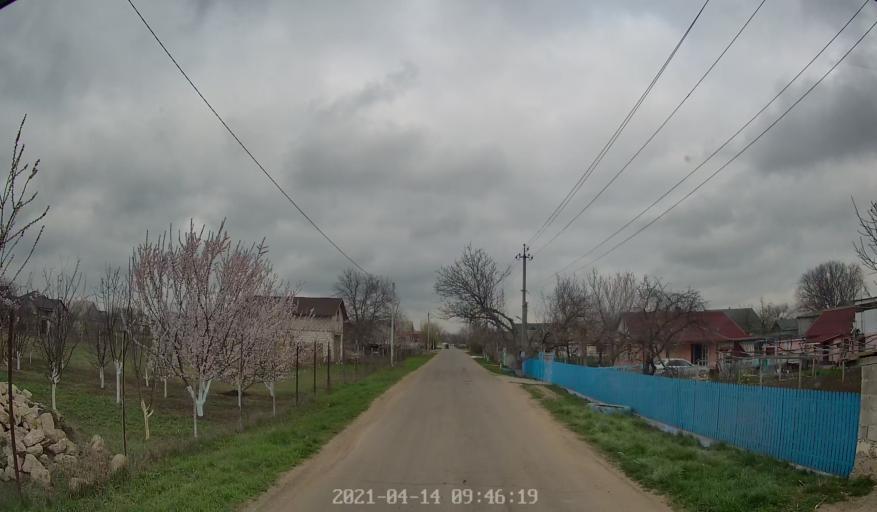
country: MD
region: Chisinau
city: Vadul lui Voda
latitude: 47.1344
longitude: 29.1234
